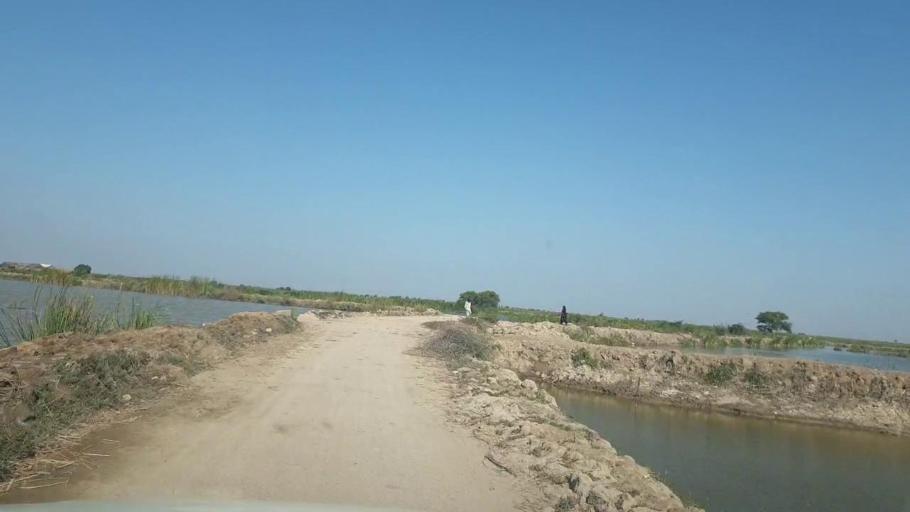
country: PK
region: Sindh
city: Chuhar Jamali
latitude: 24.4676
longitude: 67.8613
